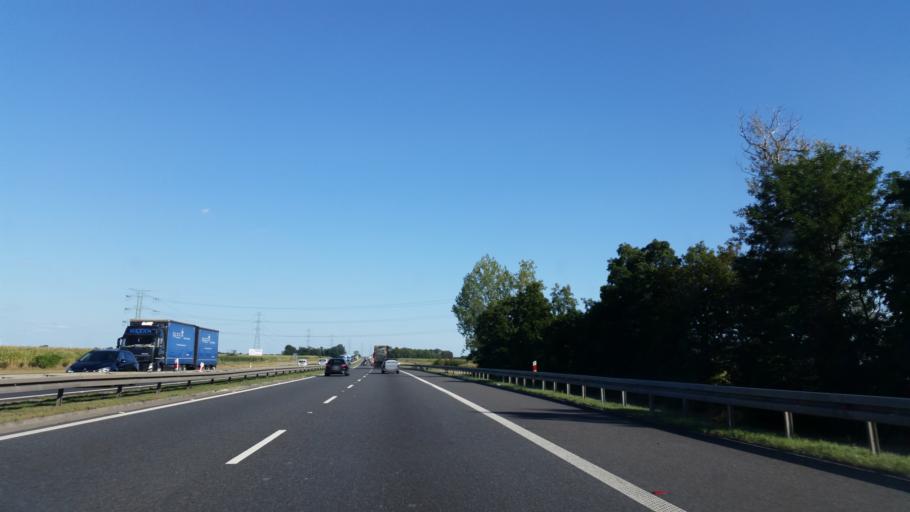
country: PL
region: Lower Silesian Voivodeship
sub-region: Powiat wroclawski
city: Zorawina
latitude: 50.9447
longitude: 17.0934
